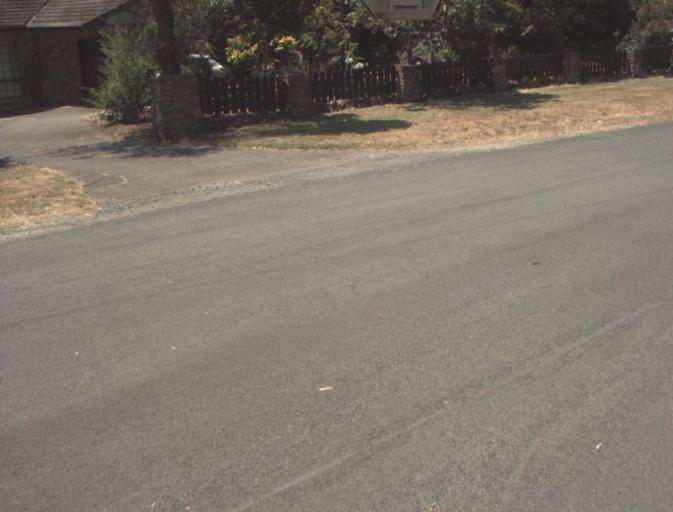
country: AU
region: Tasmania
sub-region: Launceston
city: Newstead
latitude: -41.4868
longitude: 147.1834
